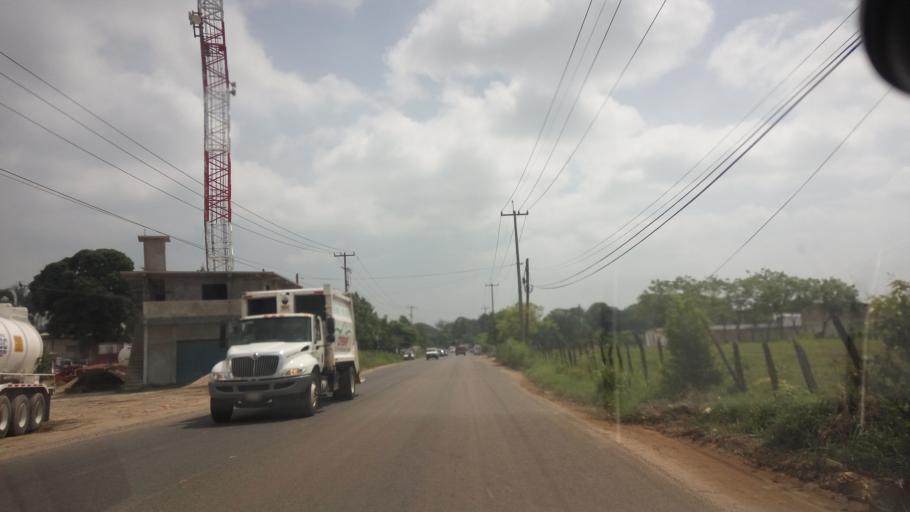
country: MX
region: Chiapas
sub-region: Reforma
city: El Carmen (El Limon)
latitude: 17.8837
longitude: -93.1466
